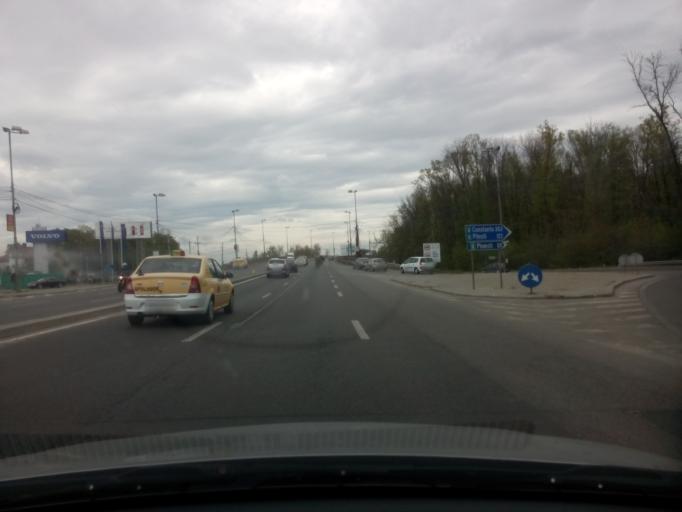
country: RO
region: Ilfov
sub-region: Comuna Otopeni
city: Otopeni
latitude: 44.5311
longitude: 26.0694
